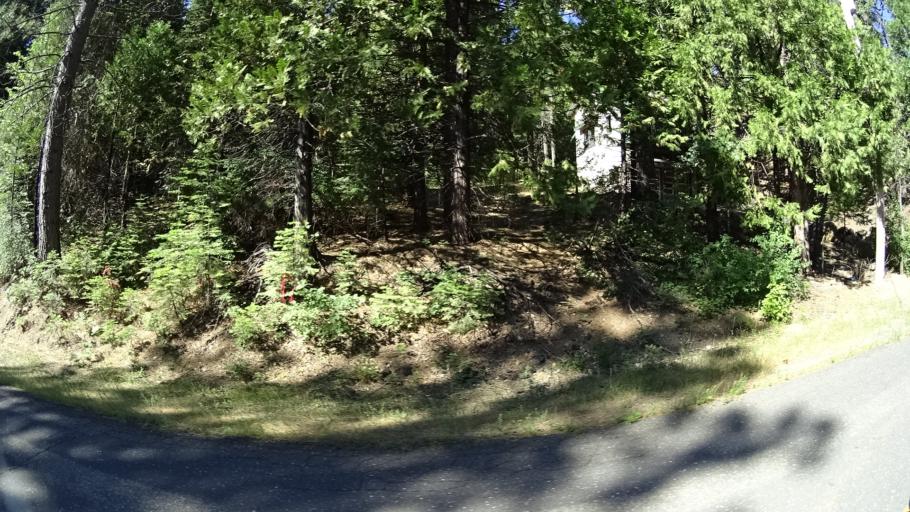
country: US
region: California
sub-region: Calaveras County
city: Arnold
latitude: 38.2858
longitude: -120.2714
